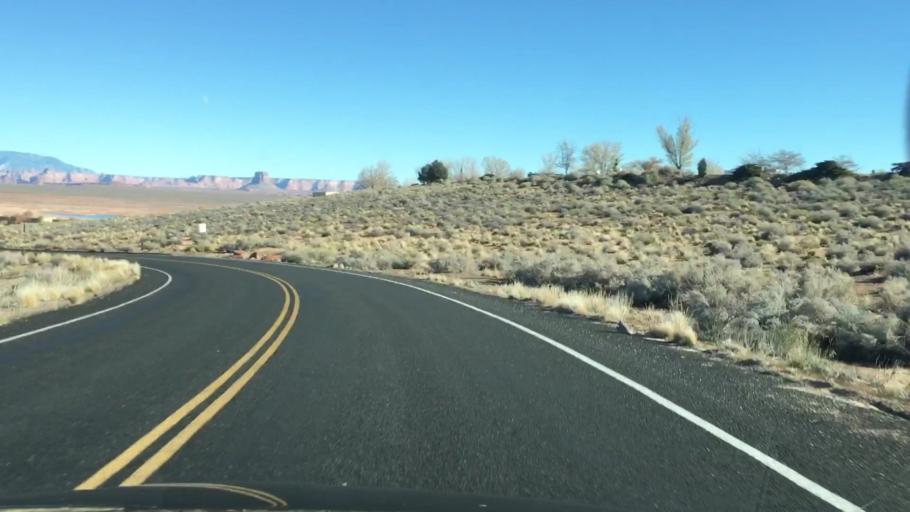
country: US
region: Arizona
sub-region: Coconino County
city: Page
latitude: 36.9934
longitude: -111.4970
